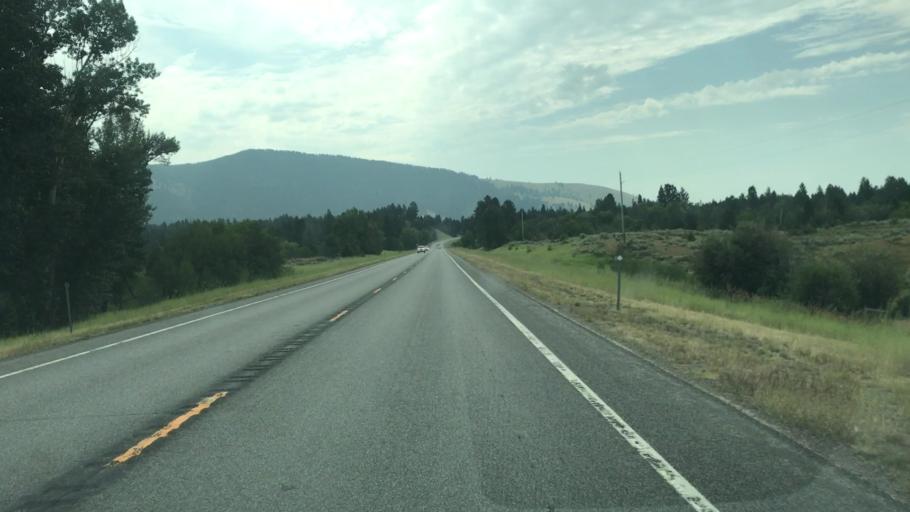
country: US
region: Montana
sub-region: Lewis and Clark County
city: Lincoln
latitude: 46.9836
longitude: -112.9996
